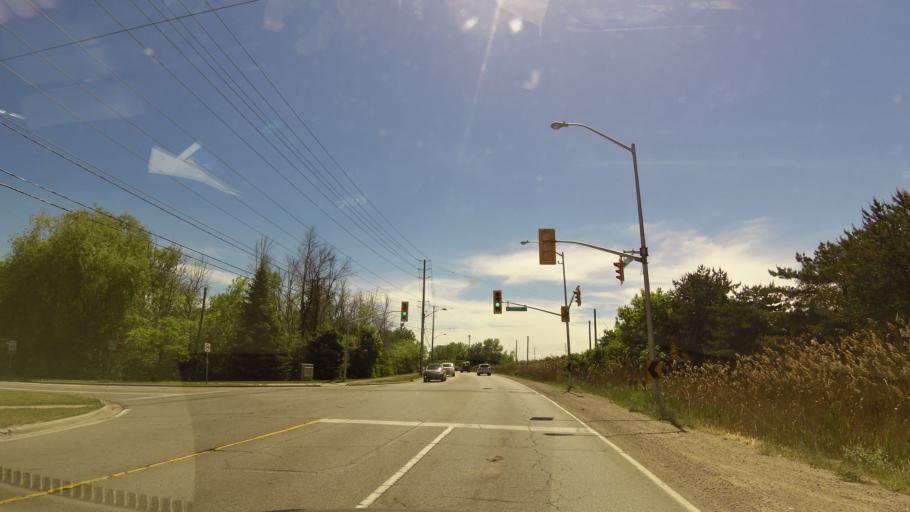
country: CA
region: Ontario
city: Oakville
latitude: 43.4713
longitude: -79.6676
